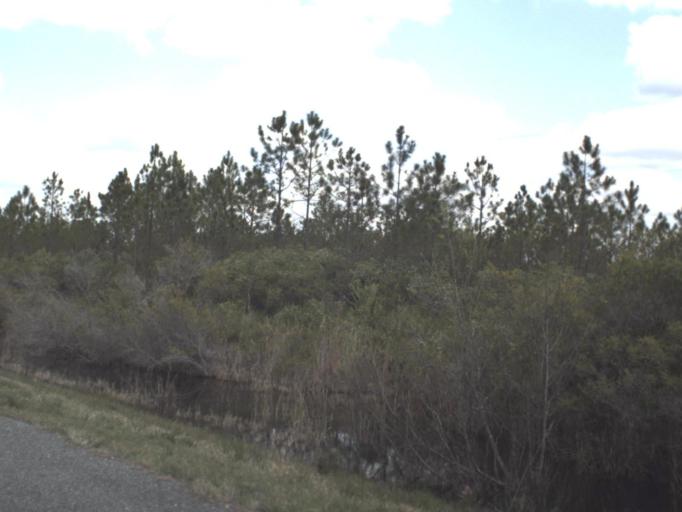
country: US
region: Florida
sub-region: Franklin County
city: Eastpoint
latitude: 29.7977
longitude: -84.8307
